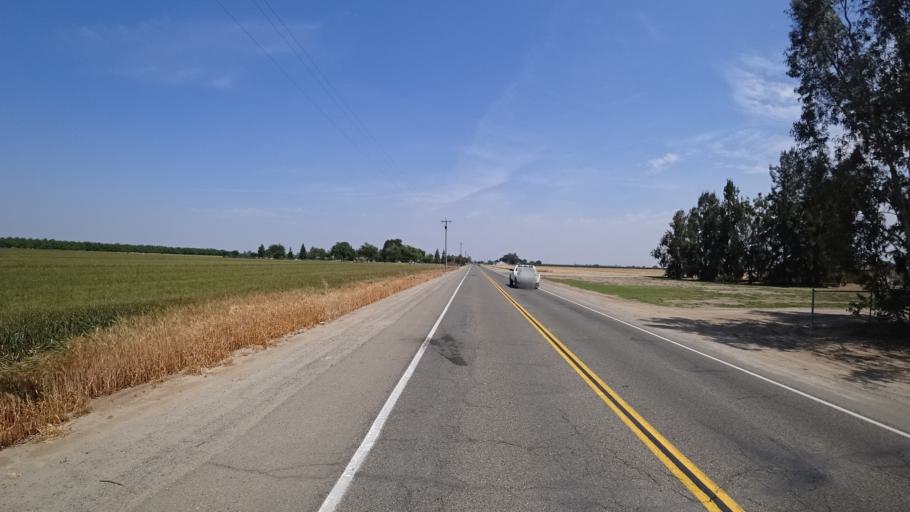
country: US
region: California
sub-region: Kings County
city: Lemoore
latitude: 36.3302
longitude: -119.7809
